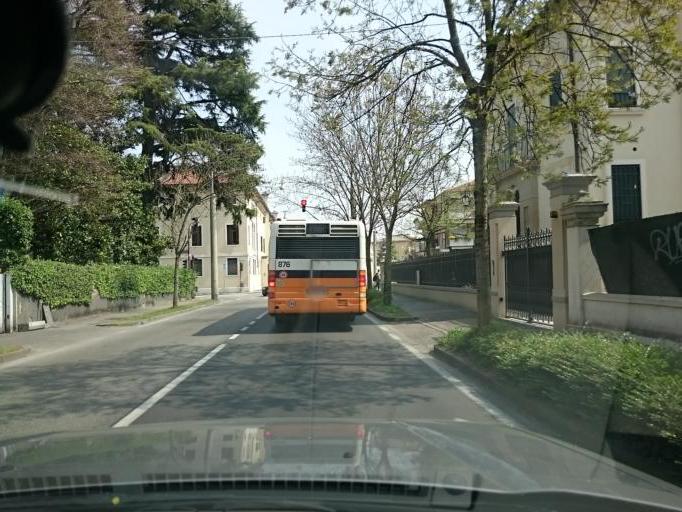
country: IT
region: Veneto
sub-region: Provincia di Padova
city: Padova
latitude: 45.3993
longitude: 11.8683
